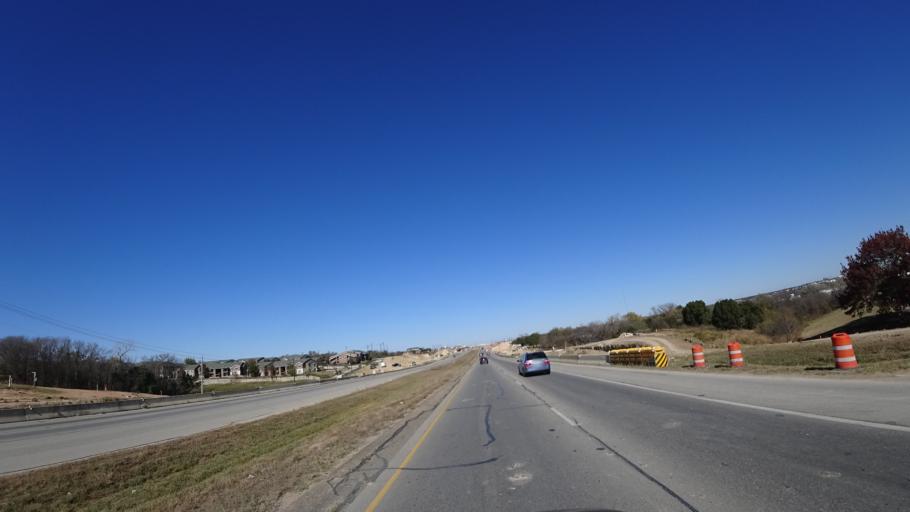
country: US
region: Texas
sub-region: Travis County
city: Austin
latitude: 30.2775
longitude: -97.6674
